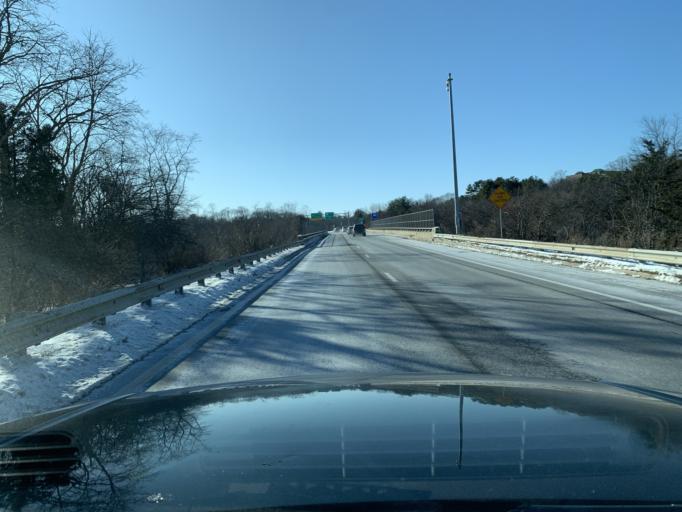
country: US
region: Massachusetts
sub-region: Essex County
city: Danvers
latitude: 42.5964
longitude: -70.9625
